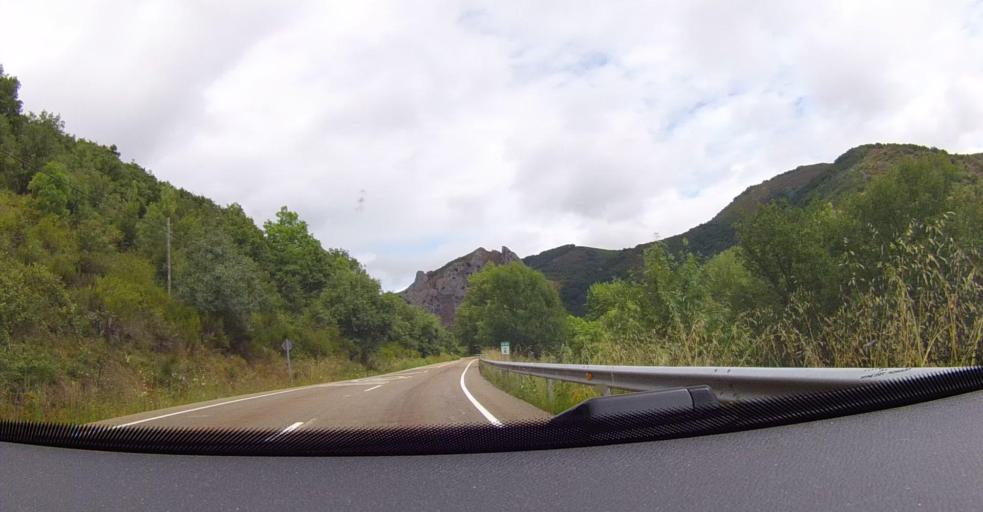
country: ES
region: Castille and Leon
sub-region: Provincia de Leon
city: Bonar
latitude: 42.8998
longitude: -5.3143
